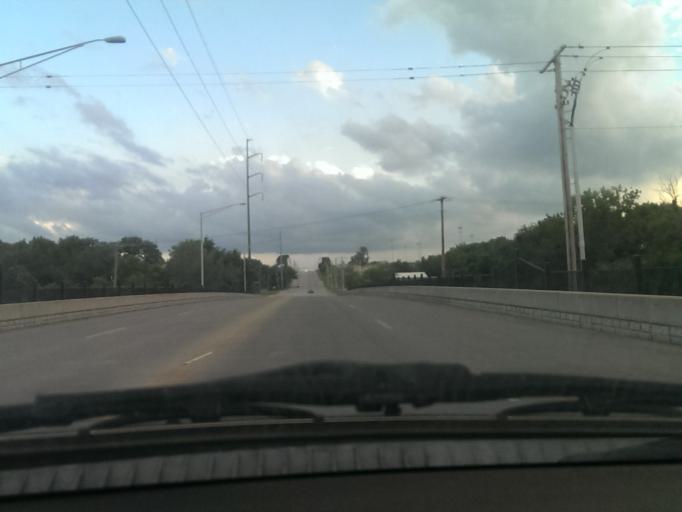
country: US
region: Kansas
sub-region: Johnson County
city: Leawood
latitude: 38.9739
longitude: -94.5765
